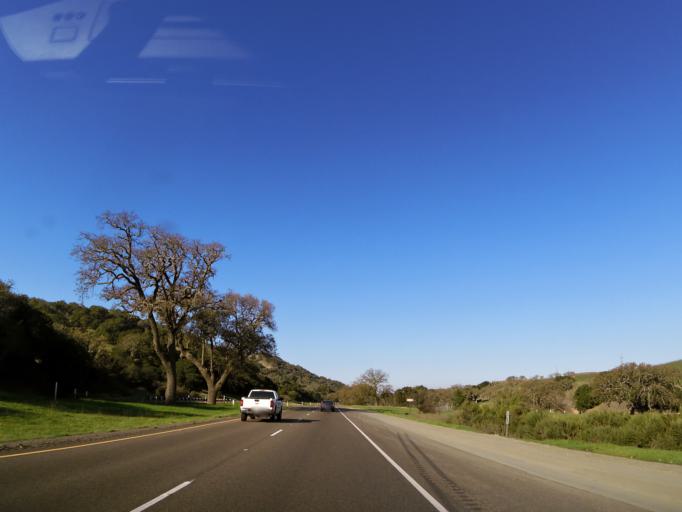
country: US
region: California
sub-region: Santa Barbara County
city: Los Alamos
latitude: 34.7178
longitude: -120.1989
